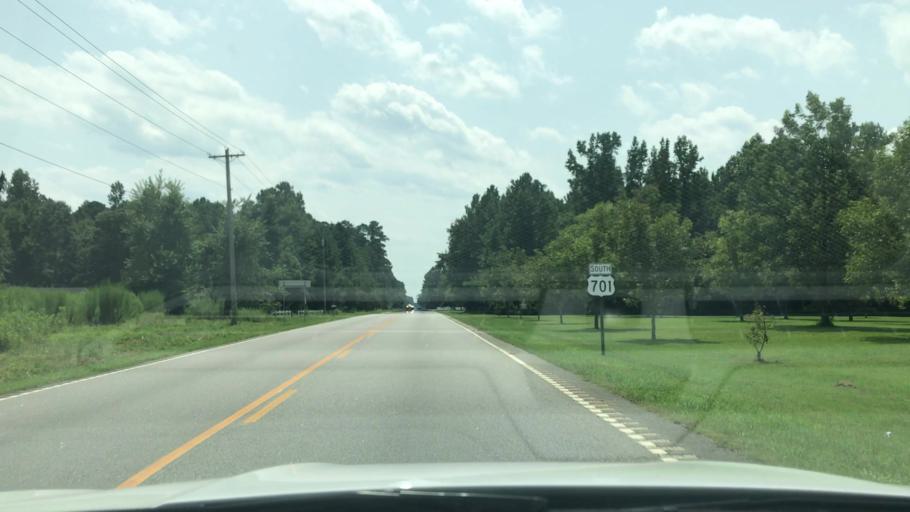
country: US
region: South Carolina
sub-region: Horry County
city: Conway
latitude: 33.7476
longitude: -79.0785
